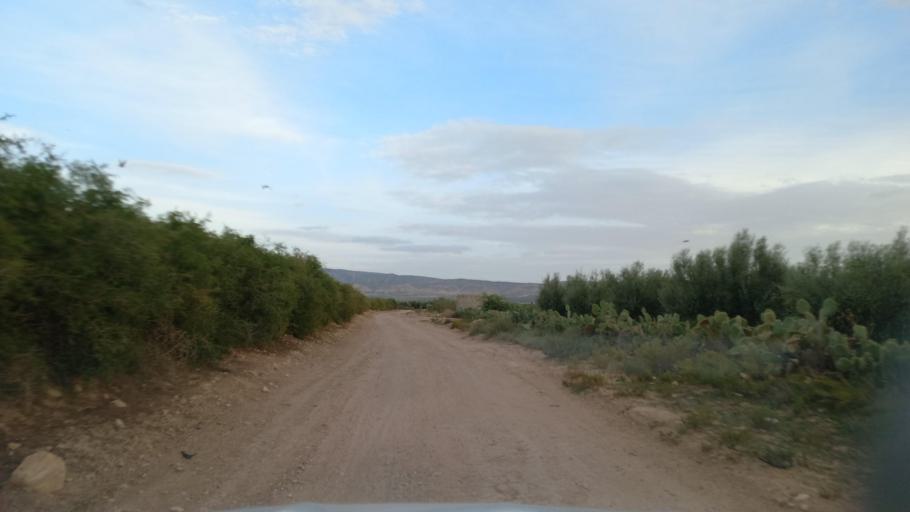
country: TN
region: Al Qasrayn
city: Sbiba
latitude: 35.4222
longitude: 9.1056
